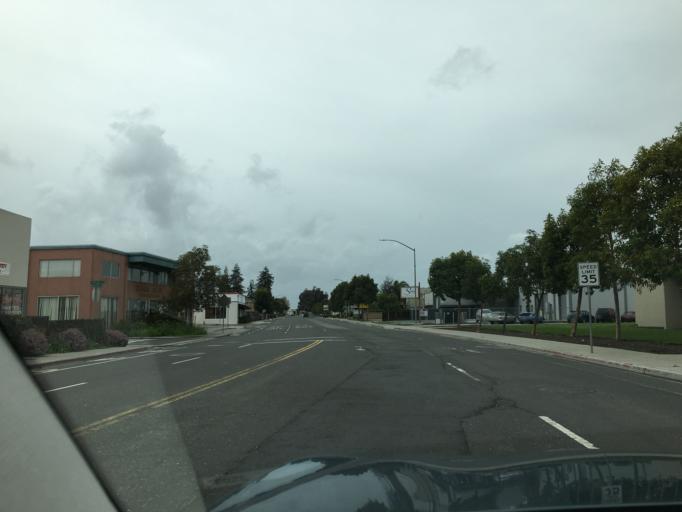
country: US
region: California
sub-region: San Mateo County
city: San Carlos
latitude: 37.5081
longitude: -122.2524
